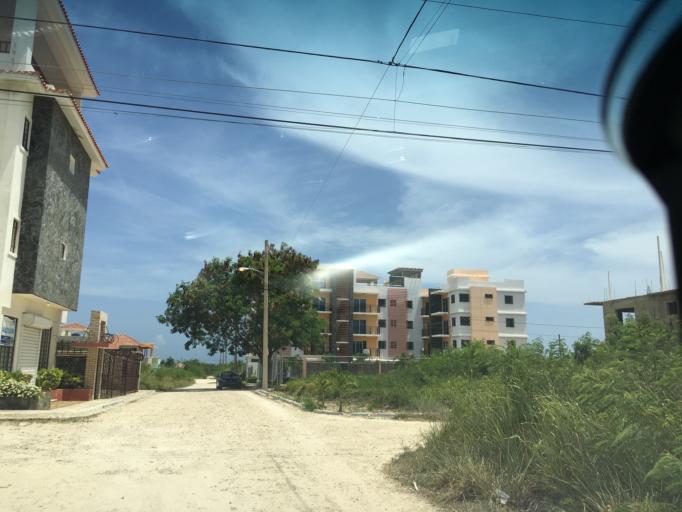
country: DO
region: La Romana
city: La Romana
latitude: 18.4215
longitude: -68.9928
